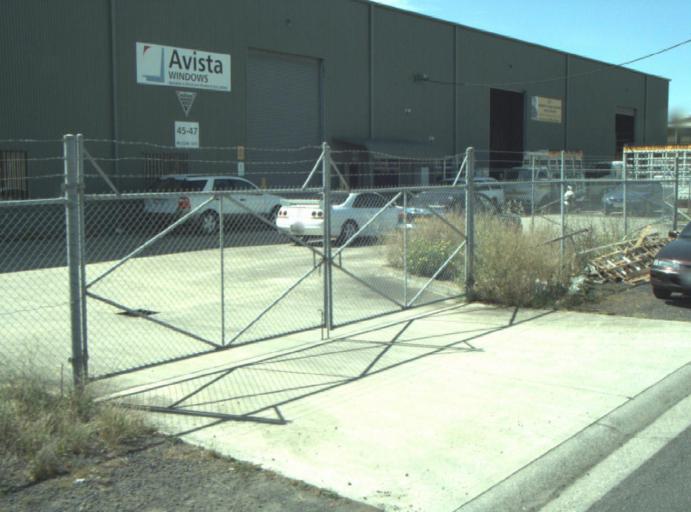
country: AU
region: Victoria
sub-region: Greater Geelong
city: East Geelong
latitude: -38.1680
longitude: 144.4157
